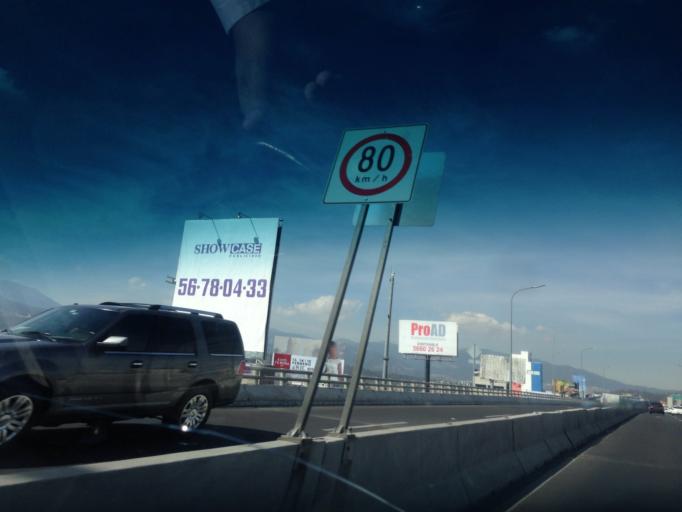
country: MX
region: Mexico City
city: Tlalpan
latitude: 19.3025
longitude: -99.1708
